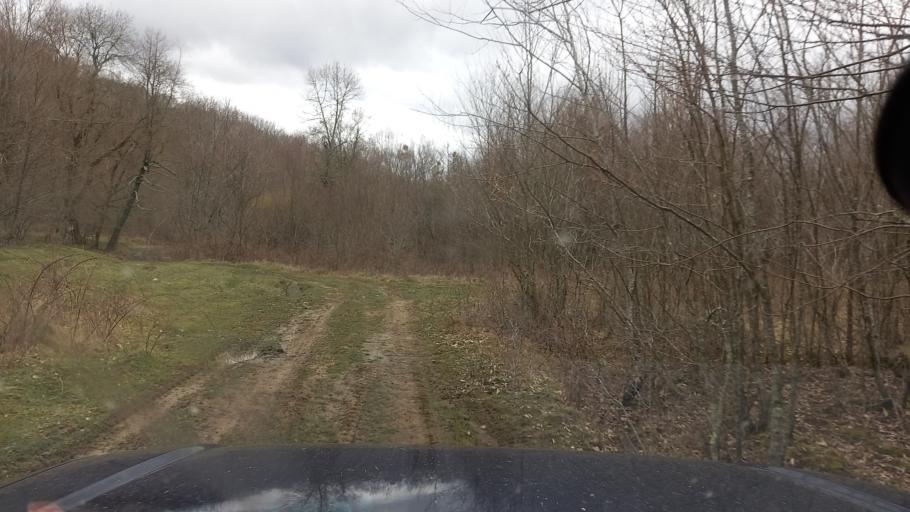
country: RU
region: Krasnodarskiy
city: Pshada
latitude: 44.4884
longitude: 38.3950
